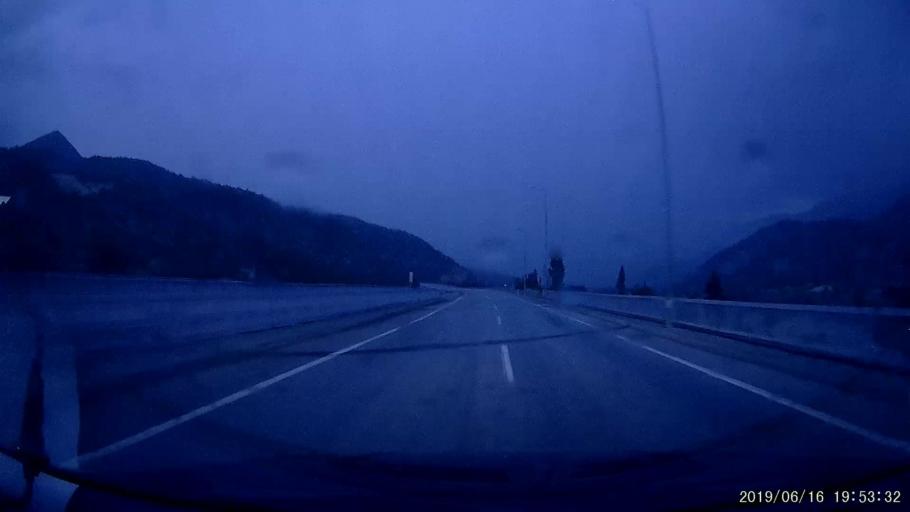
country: TR
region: Sivas
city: Koyulhisar
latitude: 40.2884
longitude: 37.7831
